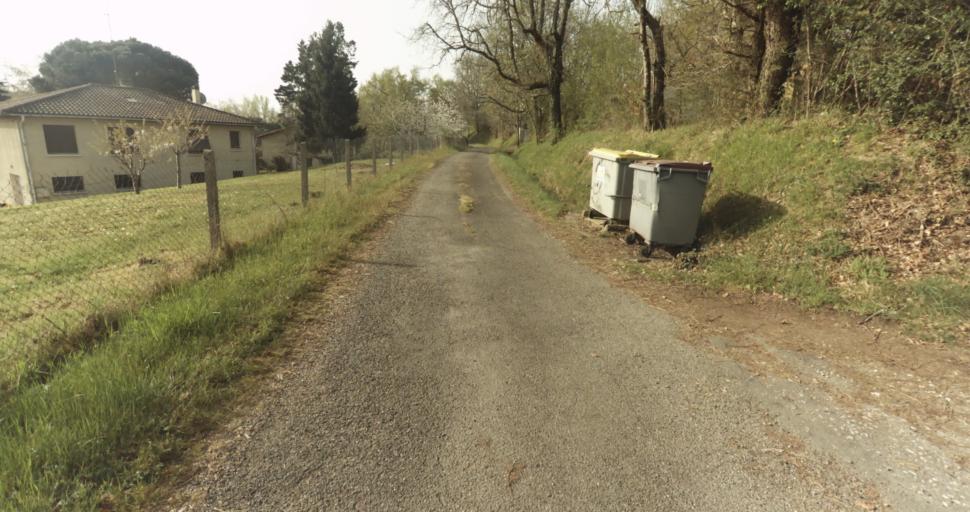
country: FR
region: Midi-Pyrenees
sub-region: Departement du Tarn-et-Garonne
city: Moissac
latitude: 44.1388
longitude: 1.1025
